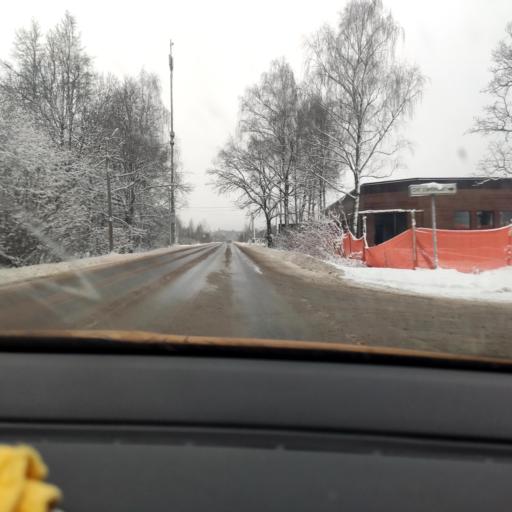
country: RU
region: Moskovskaya
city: Yershovo
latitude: 55.7552
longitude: 36.8698
